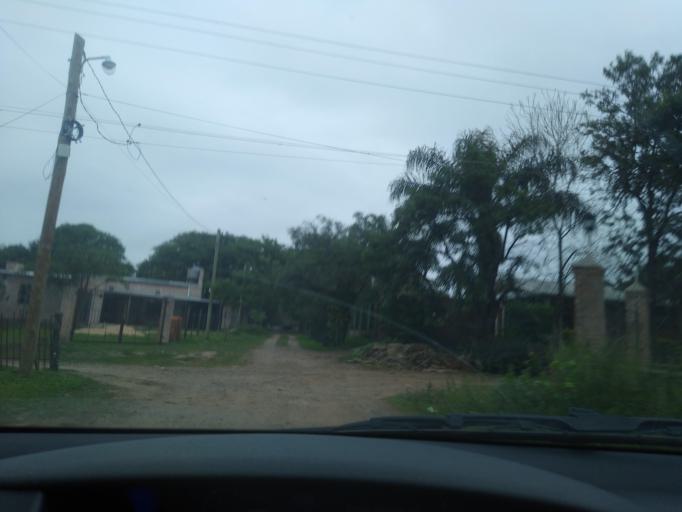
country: AR
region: Chaco
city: Colonia Benitez
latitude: -27.3322
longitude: -58.9564
